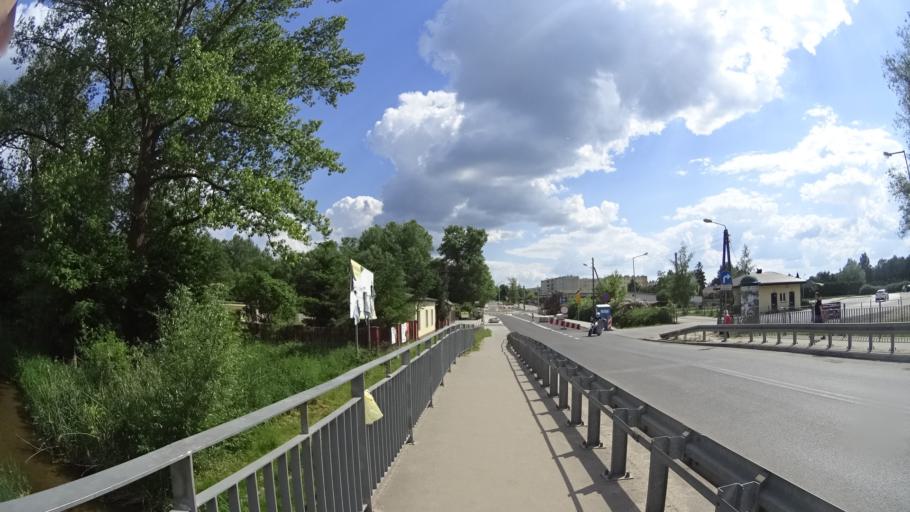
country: PL
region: Masovian Voivodeship
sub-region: Powiat piaseczynski
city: Tarczyn
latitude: 51.9770
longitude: 20.8338
